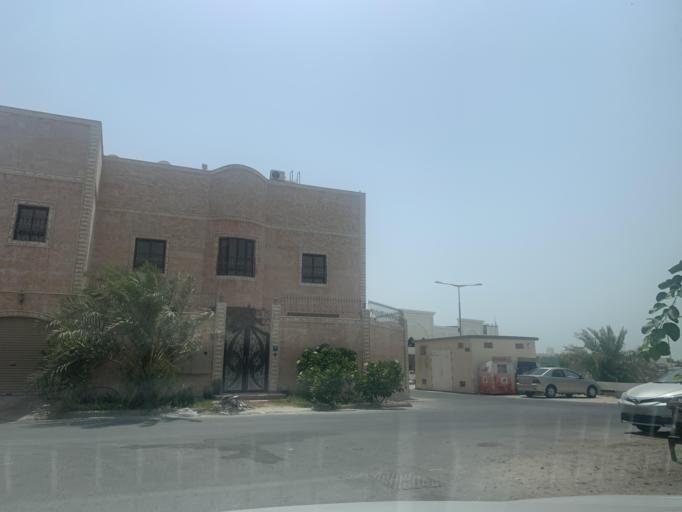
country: BH
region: Manama
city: Jidd Hafs
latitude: 26.2235
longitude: 50.4655
